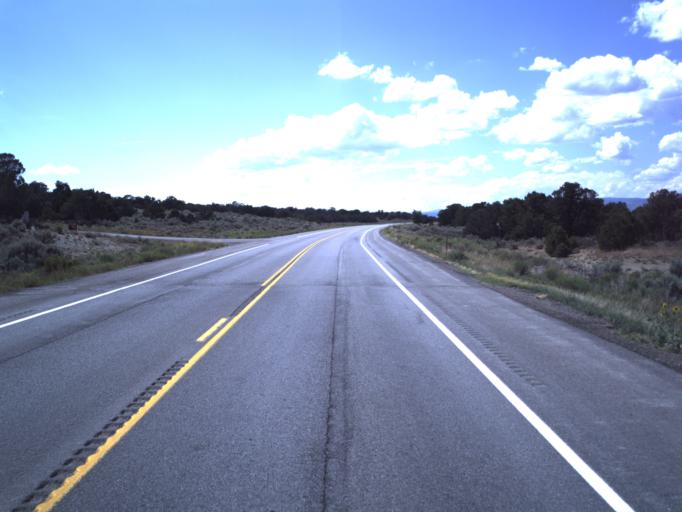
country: US
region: Utah
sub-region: Duchesne County
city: Duchesne
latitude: 40.1836
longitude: -110.6626
